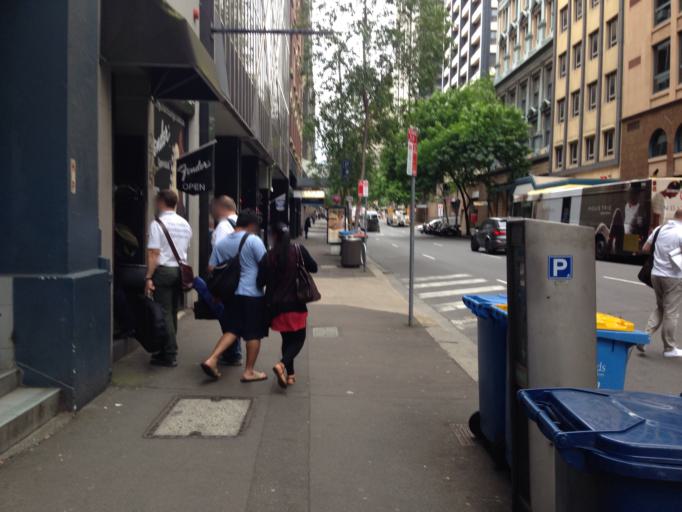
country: AU
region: New South Wales
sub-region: City of Sydney
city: Sydney
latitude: -33.8722
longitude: 151.2057
